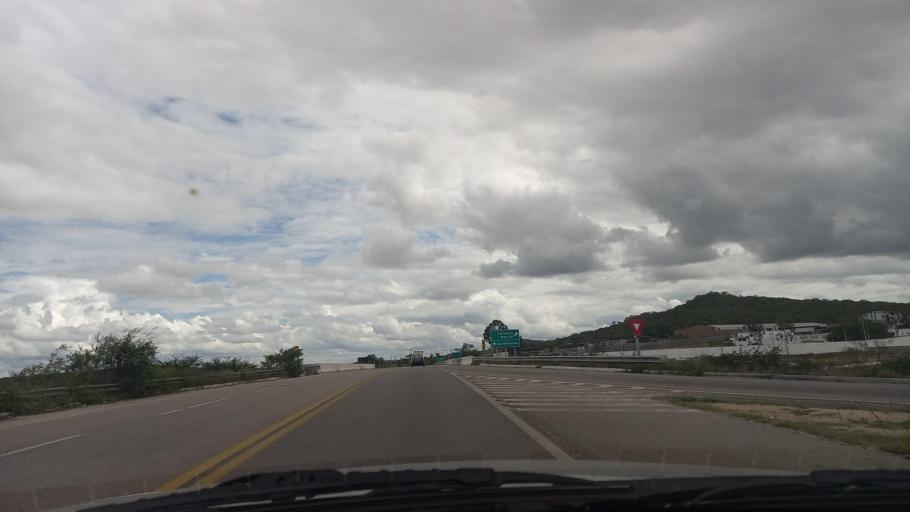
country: BR
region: Pernambuco
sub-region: Caruaru
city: Caruaru
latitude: -8.3290
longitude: -36.1458
